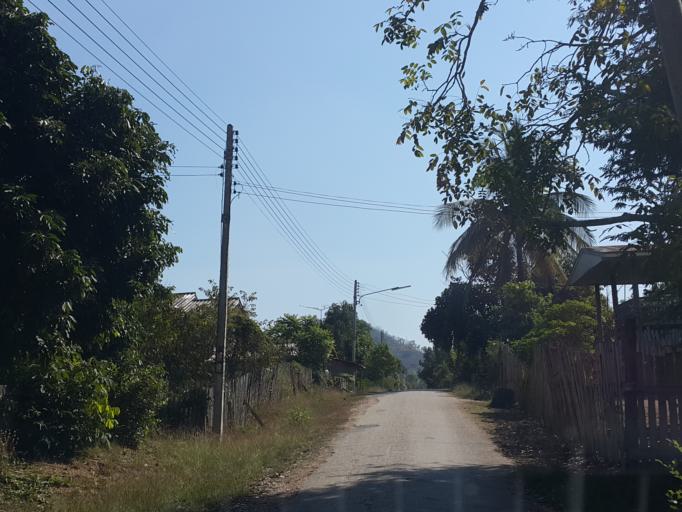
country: TH
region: Sukhothai
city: Thung Saliam
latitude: 17.3428
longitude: 99.4439
